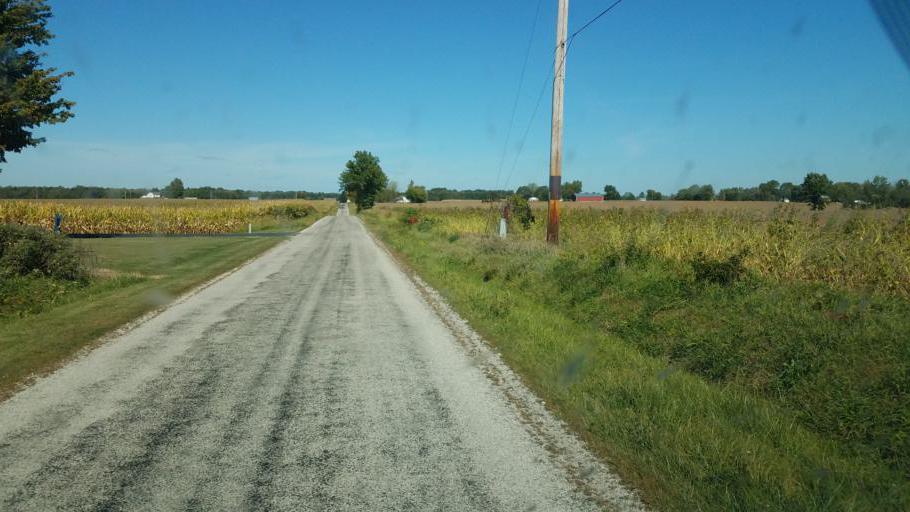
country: US
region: Ohio
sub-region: Huron County
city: Willard
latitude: 40.9540
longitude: -82.7971
